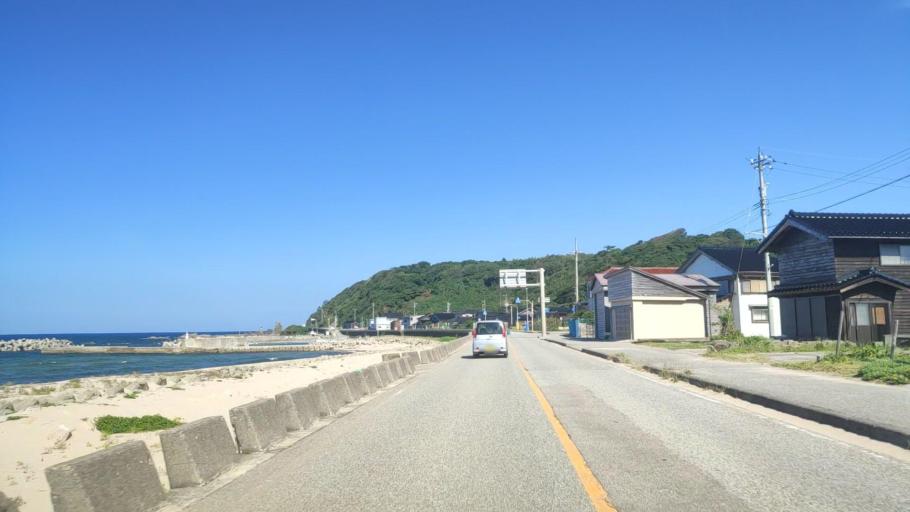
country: JP
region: Ishikawa
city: Nanao
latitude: 37.2311
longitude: 136.7054
